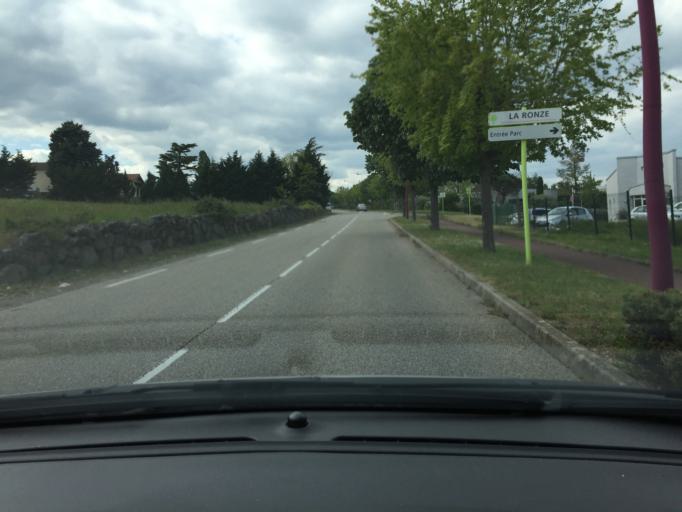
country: FR
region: Rhone-Alpes
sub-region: Departement du Rhone
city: Taluyers
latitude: 45.6343
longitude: 4.7312
